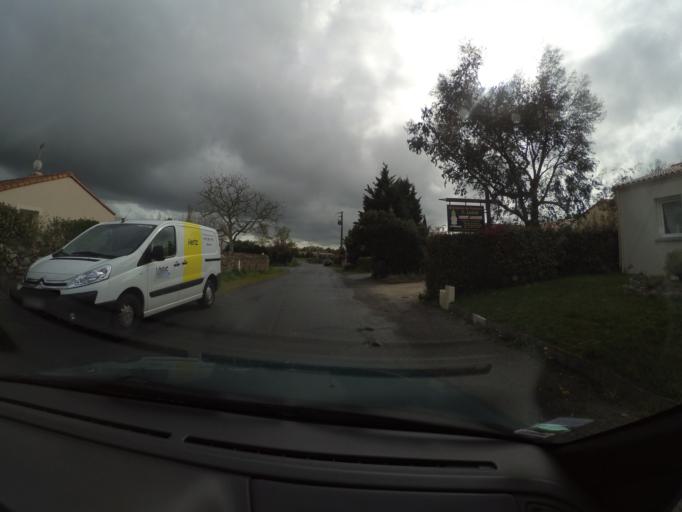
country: FR
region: Pays de la Loire
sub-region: Departement de la Loire-Atlantique
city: Maisdon-sur-Sevre
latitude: 47.0965
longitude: -1.3653
